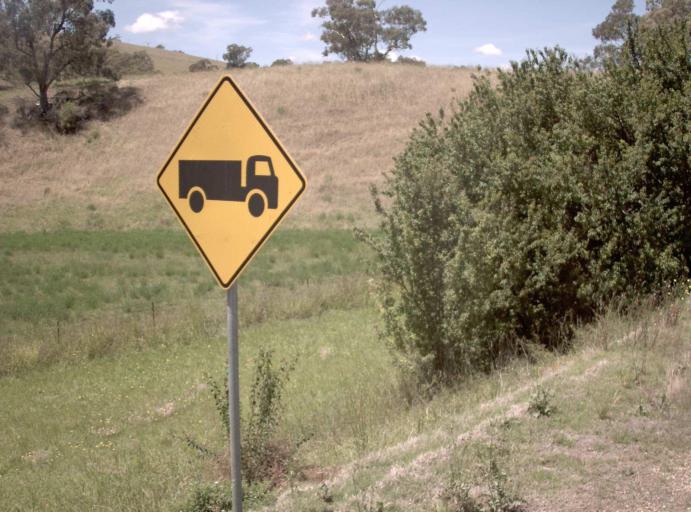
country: AU
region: Victoria
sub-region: East Gippsland
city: Bairnsdale
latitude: -37.3826
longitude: 147.8306
